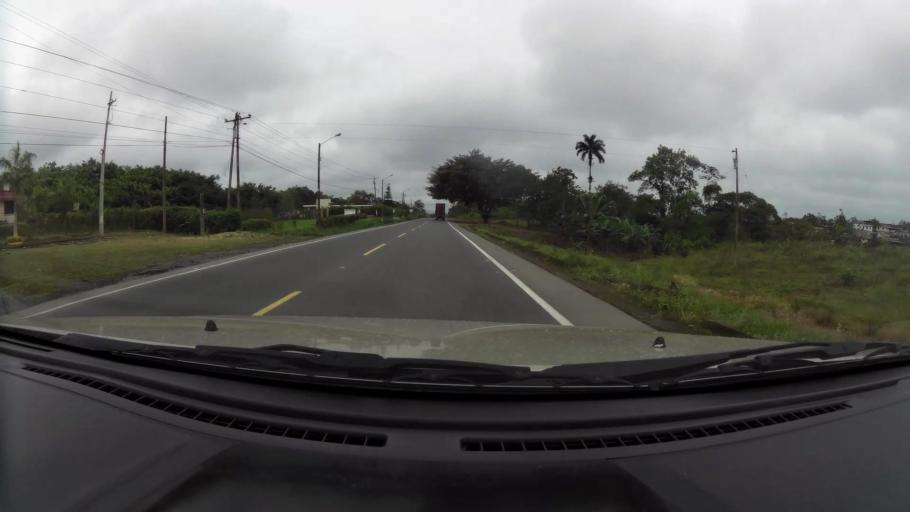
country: EC
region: Santo Domingo de los Tsachilas
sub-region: Canton Santo Domingo de los Colorados
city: Santo Domingo de los Colorados
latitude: -0.2712
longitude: -79.1546
